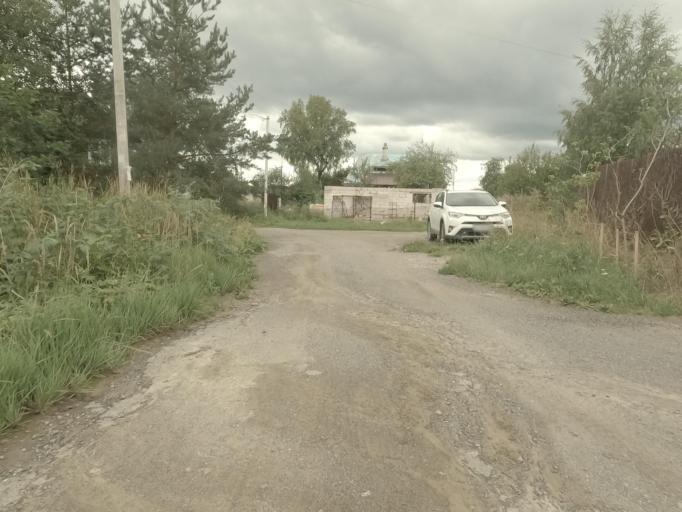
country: RU
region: Leningrad
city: Koltushi
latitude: 59.8872
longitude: 30.6945
